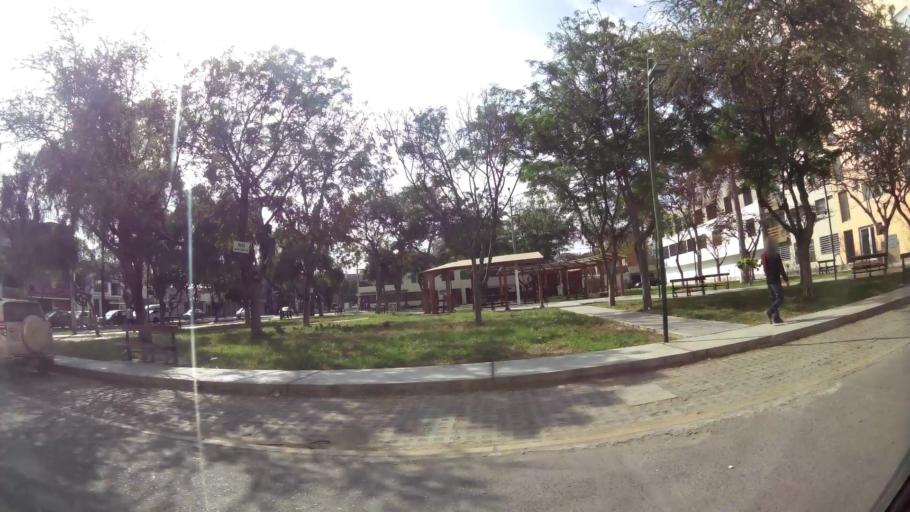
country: PE
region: La Libertad
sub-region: Provincia de Trujillo
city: Trujillo
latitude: -8.1217
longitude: -79.0184
